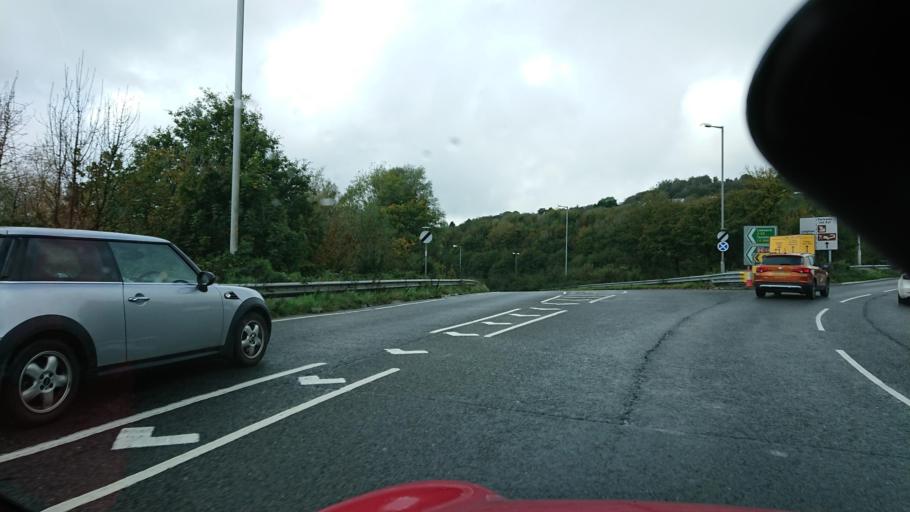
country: GB
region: England
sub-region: Plymouth
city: Plymstock
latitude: 50.3952
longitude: -4.0982
